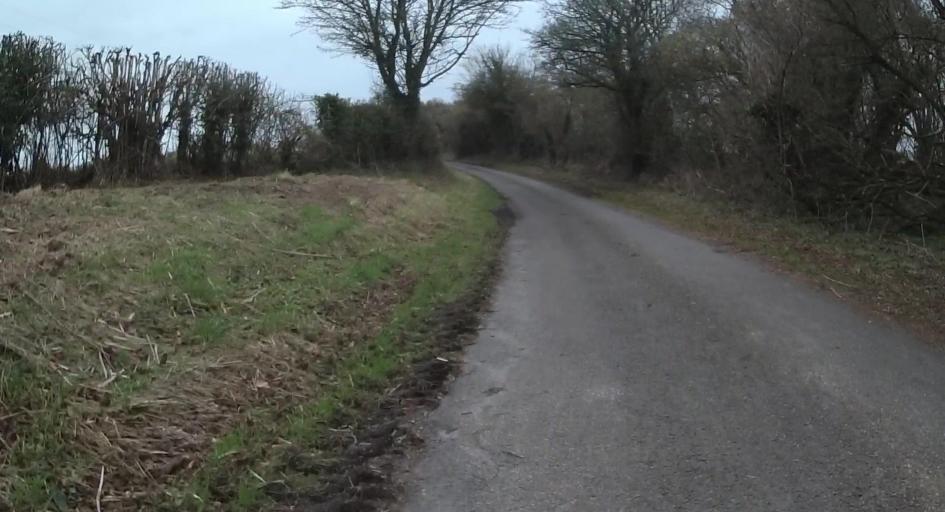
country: GB
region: England
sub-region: Hampshire
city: Highclere
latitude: 51.3257
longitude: -1.3182
